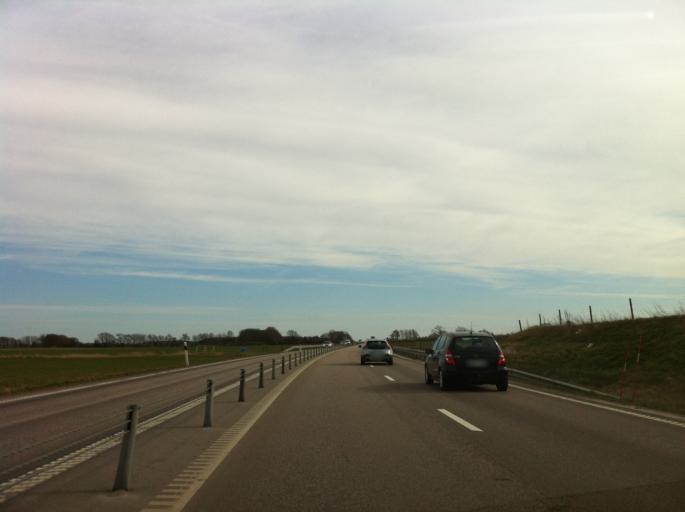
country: SE
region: Skane
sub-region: Hoganas Kommun
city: Hoganas
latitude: 56.1593
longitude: 12.5917
